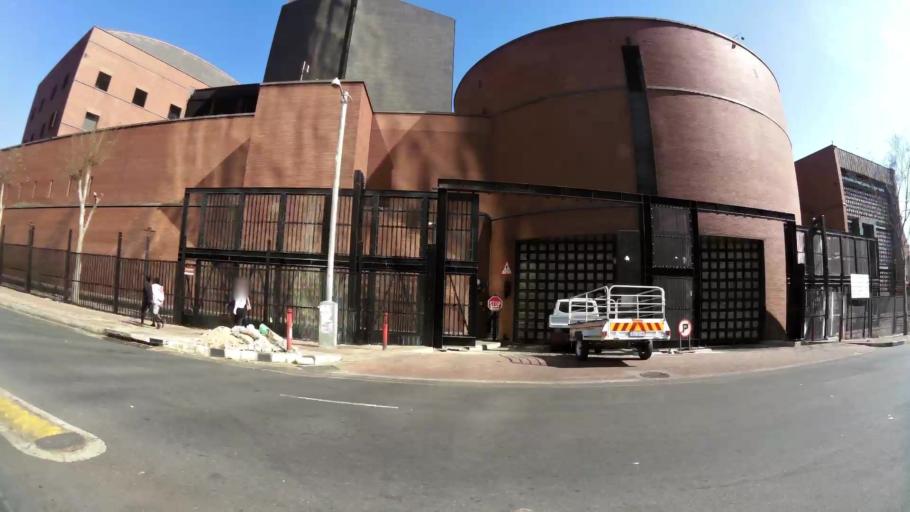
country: ZA
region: Gauteng
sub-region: City of Johannesburg Metropolitan Municipality
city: Johannesburg
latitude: -26.2041
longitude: 28.0351
